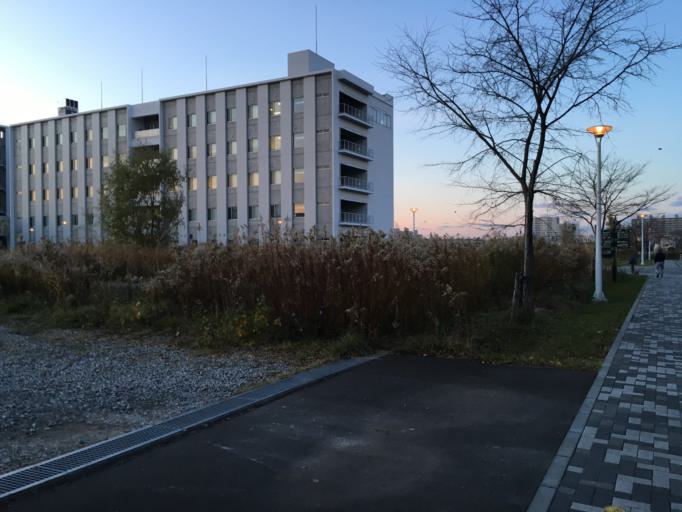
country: JP
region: Hokkaido
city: Sapporo
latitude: 43.0832
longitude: 141.3377
